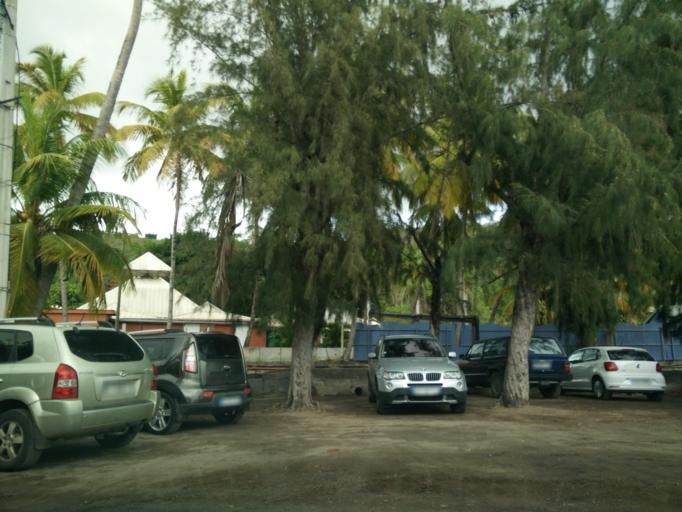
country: MQ
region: Martinique
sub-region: Martinique
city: Saint-Pierre
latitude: 14.6972
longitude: -61.1801
